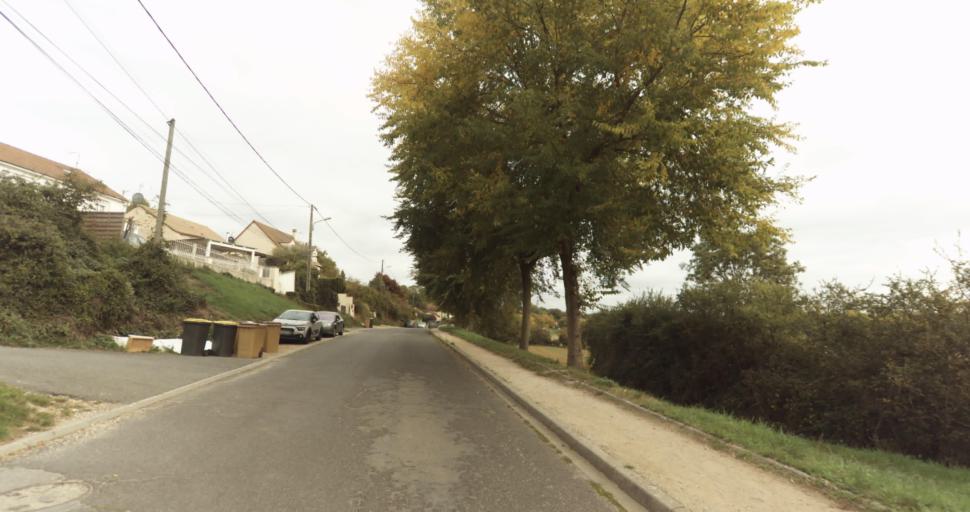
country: FR
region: Centre
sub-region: Departement d'Eure-et-Loir
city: Dreux
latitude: 48.7238
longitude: 1.3493
